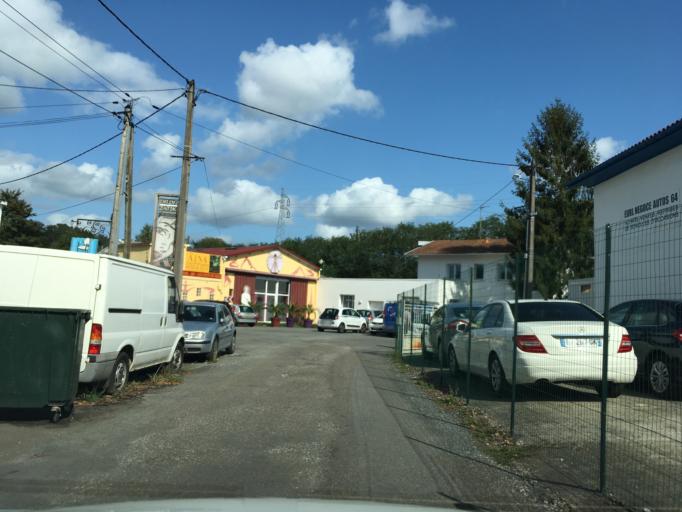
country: FR
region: Aquitaine
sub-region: Departement des Pyrenees-Atlantiques
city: Bayonne
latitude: 43.4808
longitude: -1.4749
